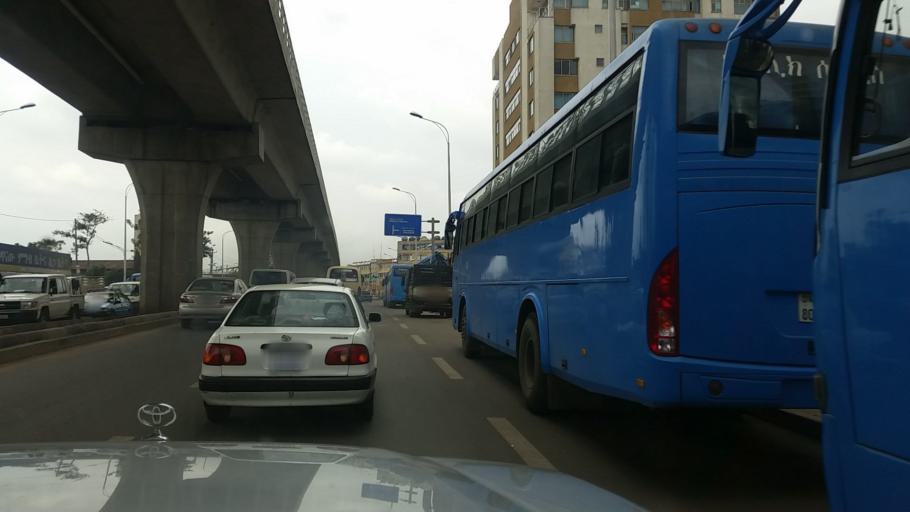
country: ET
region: Adis Abeba
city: Addis Ababa
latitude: 9.0117
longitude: 38.7515
